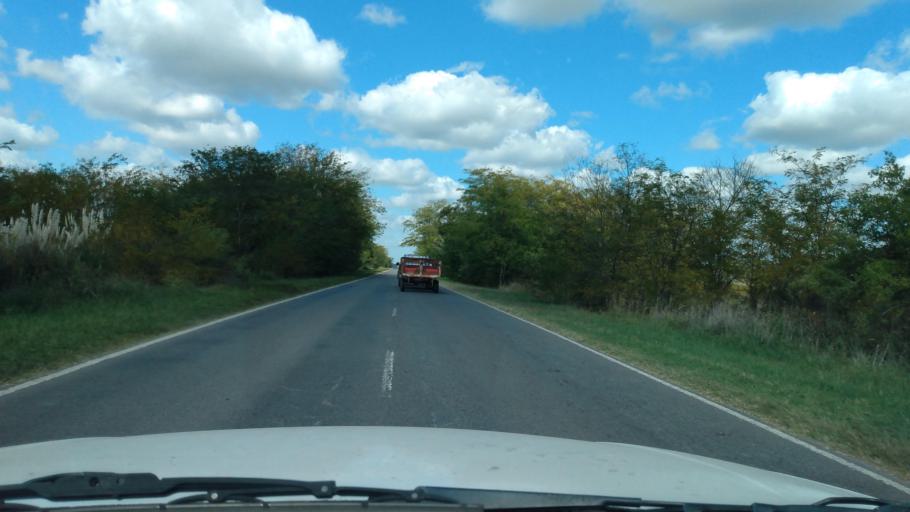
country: AR
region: Buenos Aires
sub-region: Partido de Navarro
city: Navarro
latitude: -34.9425
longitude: -59.3211
